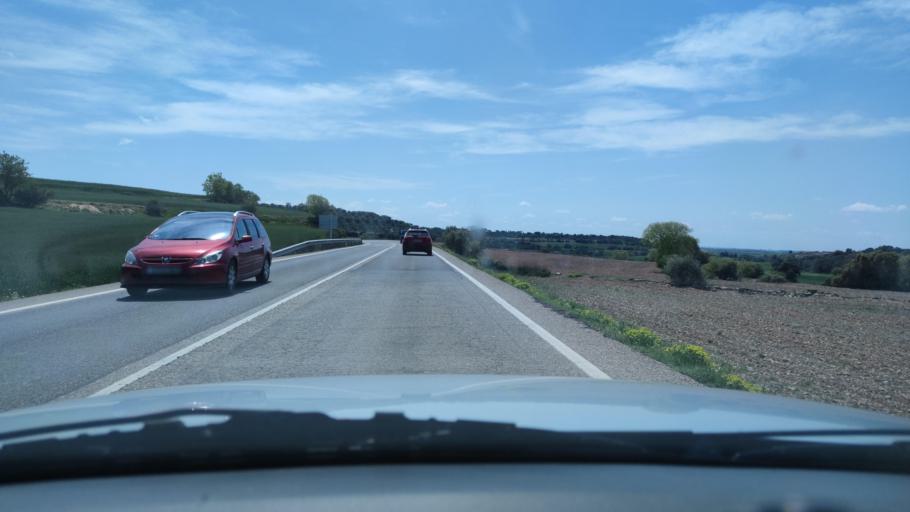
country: ES
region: Catalonia
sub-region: Provincia de Lleida
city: Tarrega
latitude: 41.6902
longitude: 1.1645
